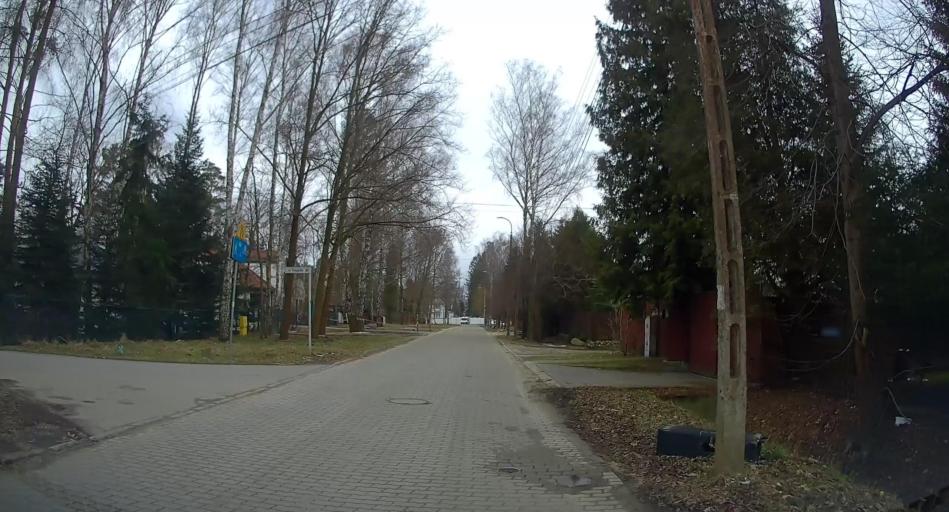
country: PL
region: Masovian Voivodeship
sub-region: Powiat piaseczynski
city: Piaseczno
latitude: 52.0622
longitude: 20.9926
